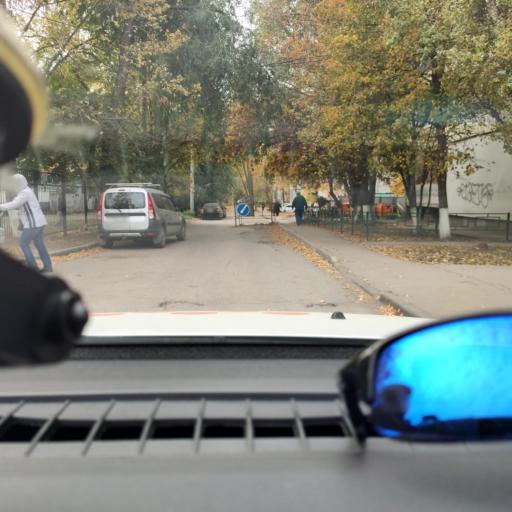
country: RU
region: Samara
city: Samara
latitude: 53.2600
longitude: 50.2302
